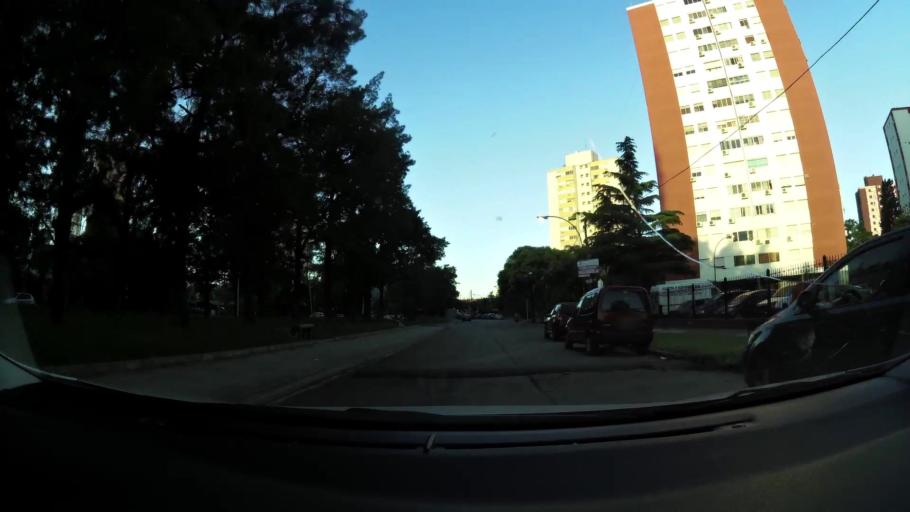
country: AR
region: Buenos Aires F.D.
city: Villa Lugano
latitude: -34.6958
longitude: -58.4768
